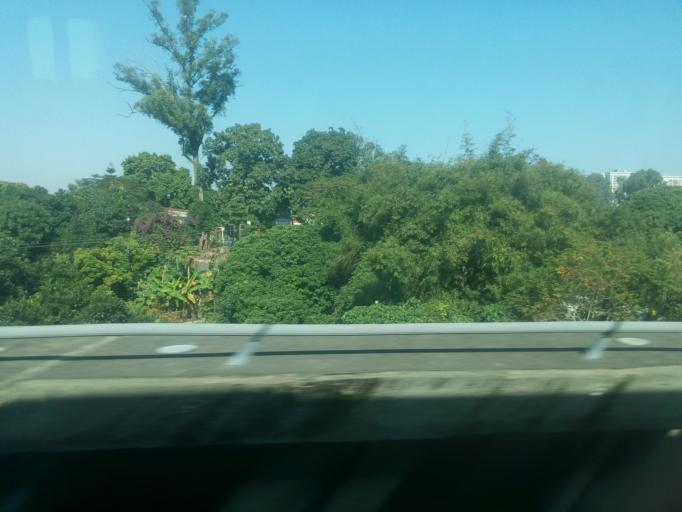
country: HK
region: Yuen Long
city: Yuen Long Kau Hui
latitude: 22.4488
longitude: 114.0186
